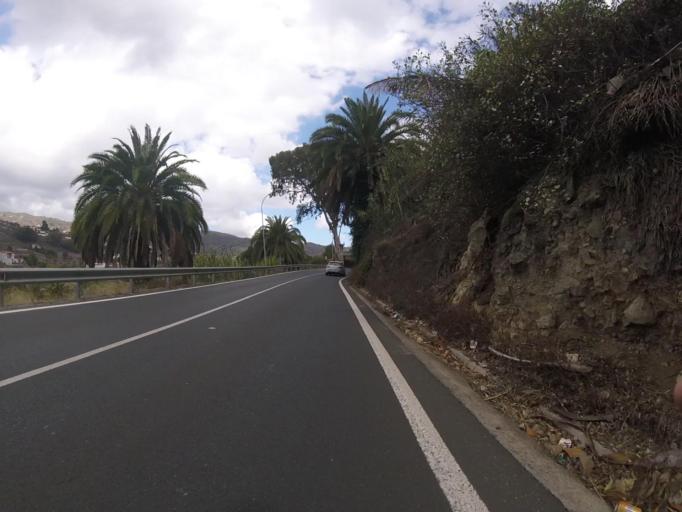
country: ES
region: Canary Islands
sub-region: Provincia de Las Palmas
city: Santa Brigida
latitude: 28.0288
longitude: -15.5002
